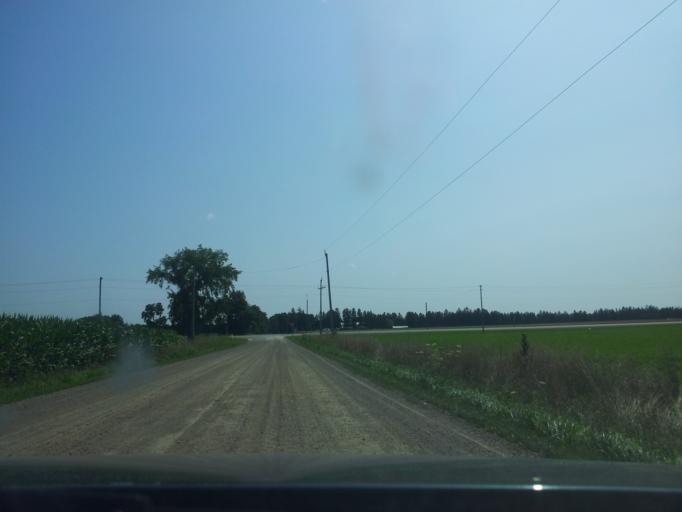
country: CA
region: Ontario
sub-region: Oxford County
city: Woodstock
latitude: 42.9584
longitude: -80.5911
